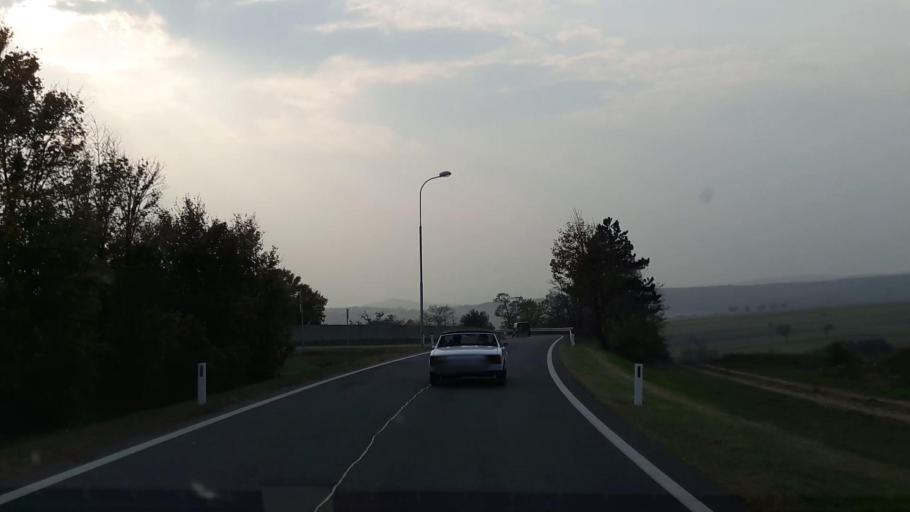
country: AT
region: Burgenland
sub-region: Politischer Bezirk Neusiedl am See
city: Neusiedl am See
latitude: 47.9737
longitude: 16.8386
